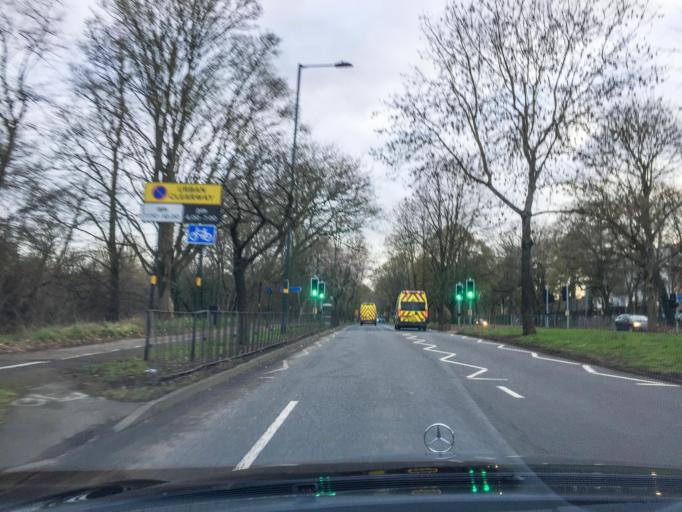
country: GB
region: England
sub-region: City and Borough of Birmingham
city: Bartley Green
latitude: 52.4292
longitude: -1.9513
